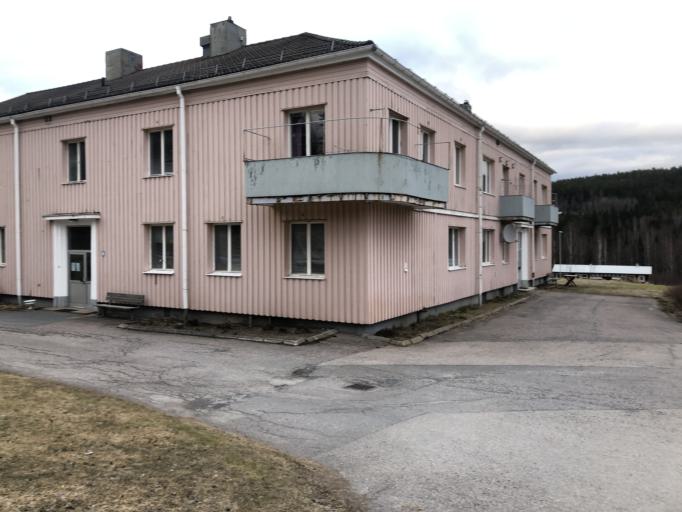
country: SE
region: Vaermland
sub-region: Filipstads Kommun
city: Lesjofors
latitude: 59.9820
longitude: 14.1758
